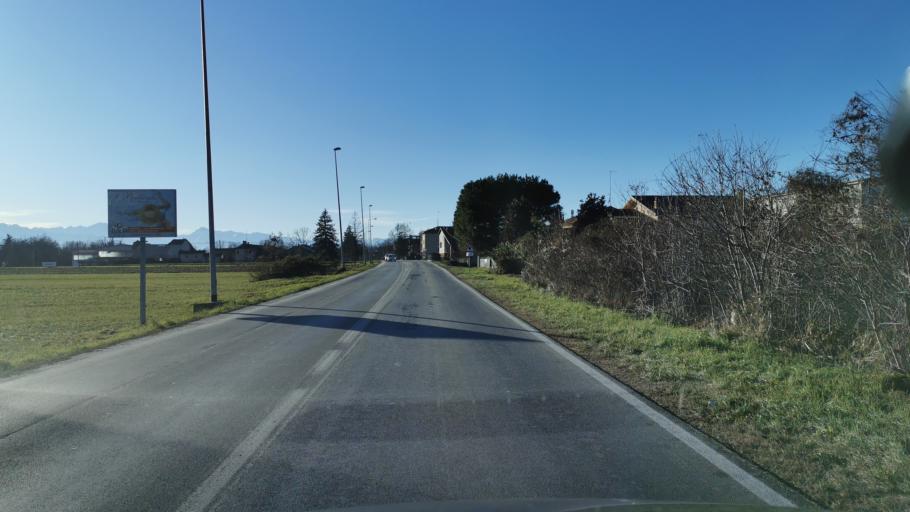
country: IT
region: Piedmont
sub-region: Provincia di Cuneo
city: Carru
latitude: 44.4737
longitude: 7.8521
